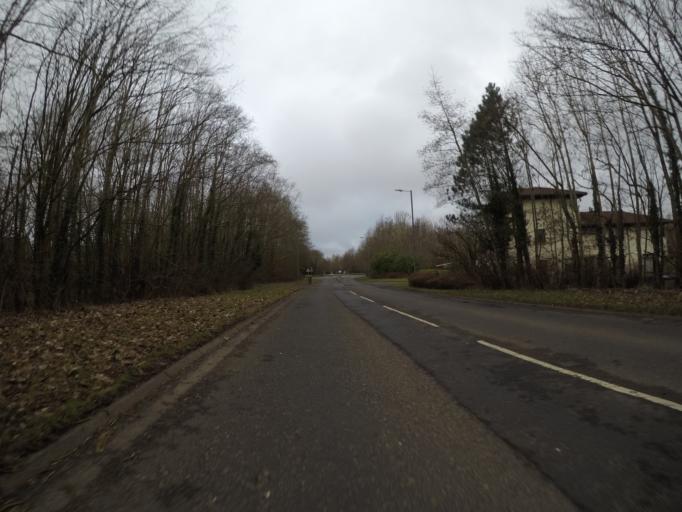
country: GB
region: Scotland
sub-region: North Ayrshire
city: Irvine
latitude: 55.6309
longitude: -4.6339
